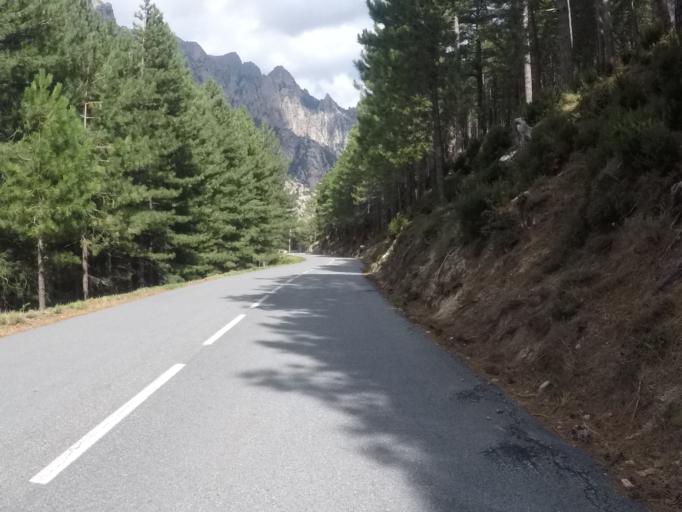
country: FR
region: Corsica
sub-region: Departement de la Corse-du-Sud
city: Zonza
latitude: 41.8007
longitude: 9.2372
